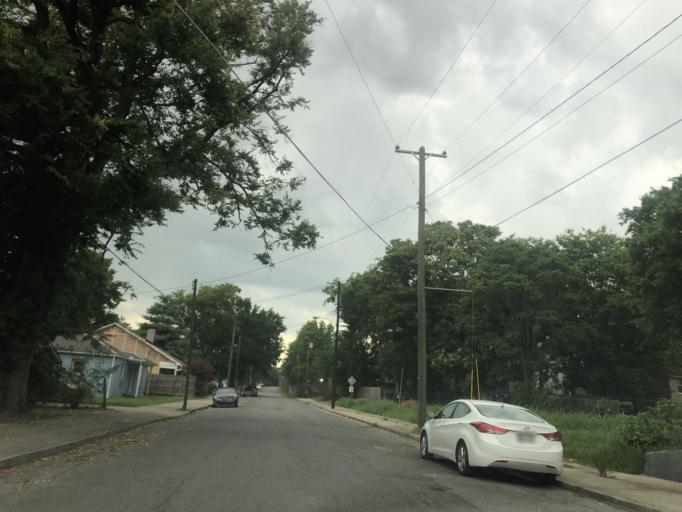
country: US
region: Tennessee
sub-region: Davidson County
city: Nashville
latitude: 36.1771
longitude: -86.8023
